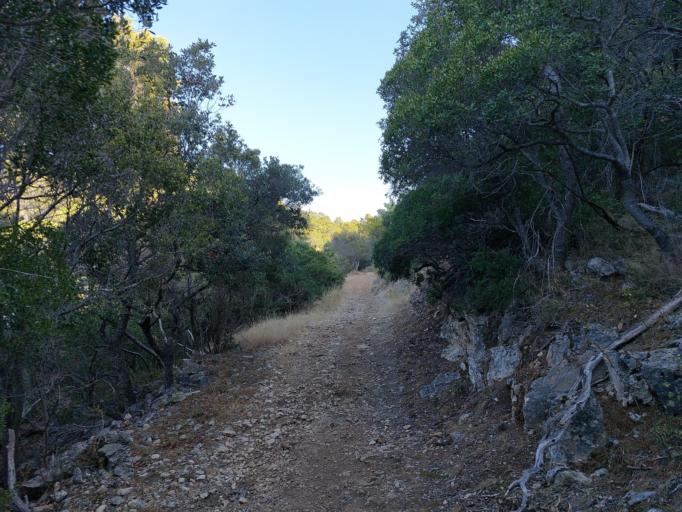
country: HR
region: Dubrovacko-Neretvanska
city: Smokvica
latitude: 42.7570
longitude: 16.8095
